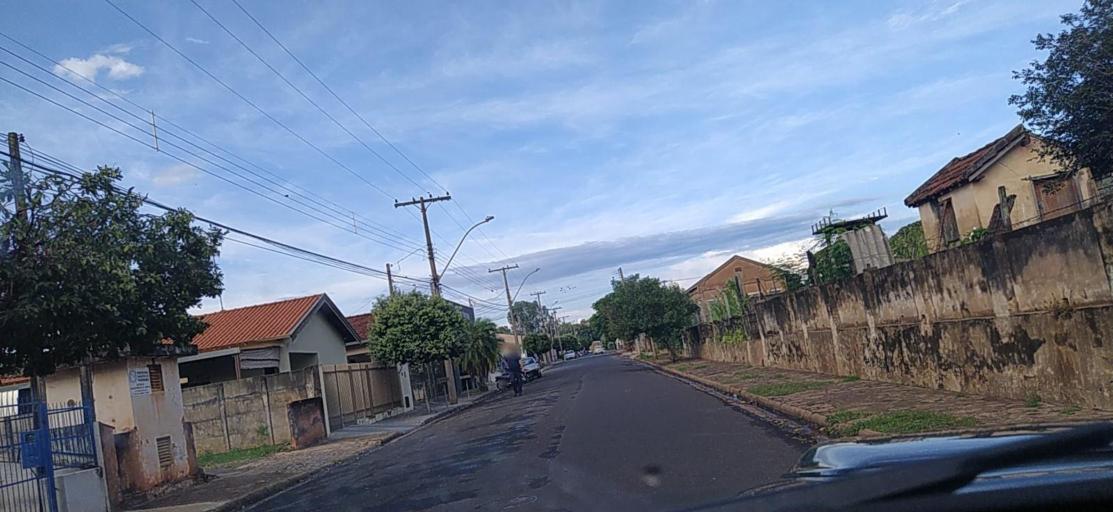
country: BR
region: Sao Paulo
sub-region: Pindorama
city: Pindorama
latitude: -21.1870
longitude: -48.9032
